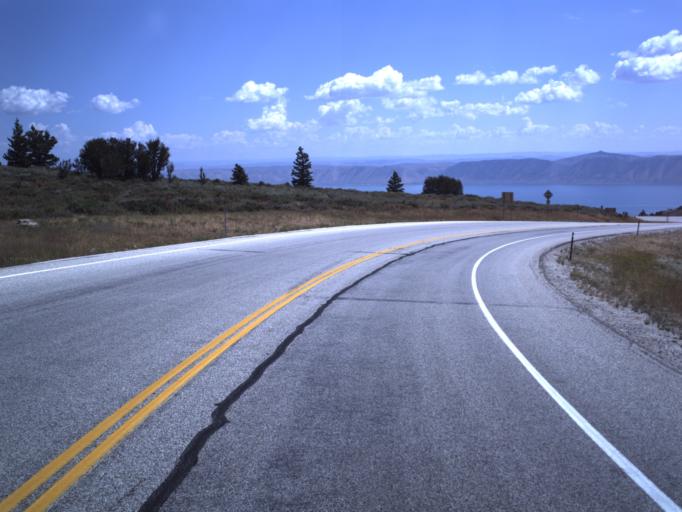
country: US
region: Idaho
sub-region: Bear Lake County
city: Paris
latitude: 41.9278
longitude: -111.4543
